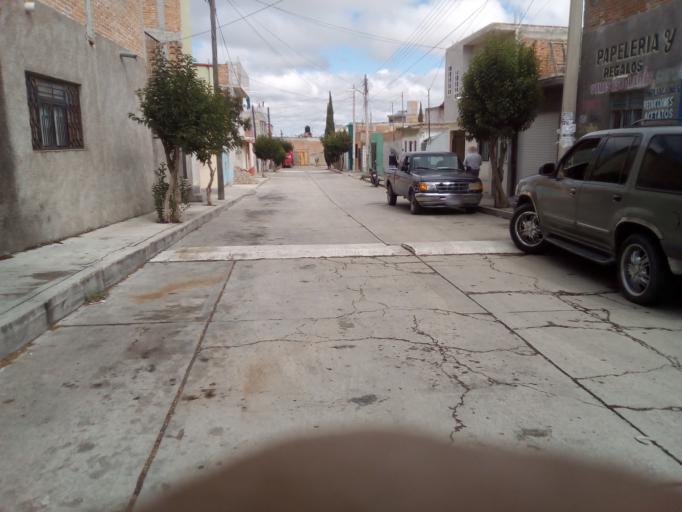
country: MX
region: Guerrero
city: San Luis de la Paz
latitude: 21.2912
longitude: -100.5117
